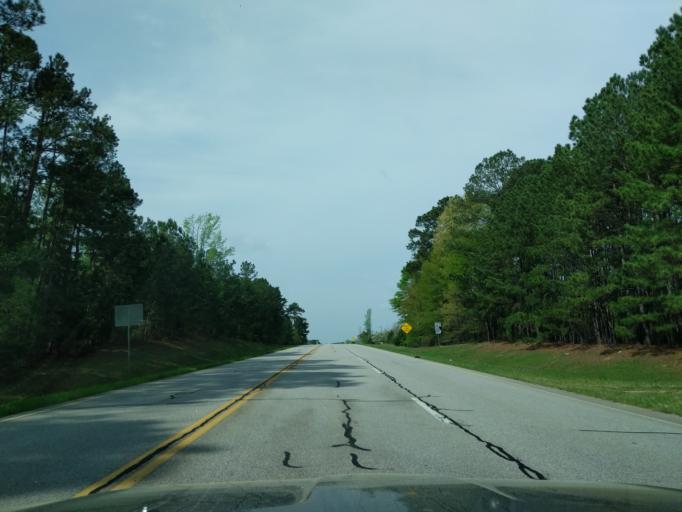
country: US
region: Georgia
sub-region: Lincoln County
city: Lincolnton
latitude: 33.8465
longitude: -82.4054
